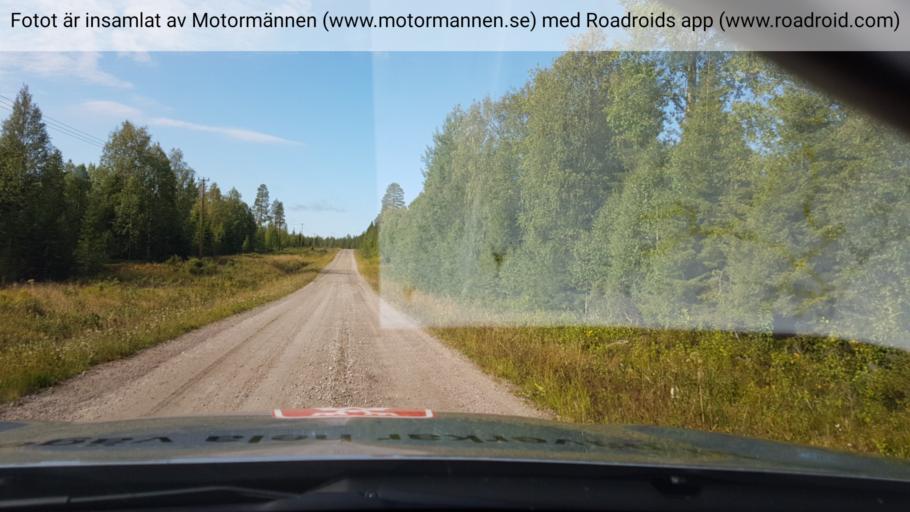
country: FI
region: Lapland
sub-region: Torniolaakso
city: Ylitornio
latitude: 66.2102
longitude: 23.4870
